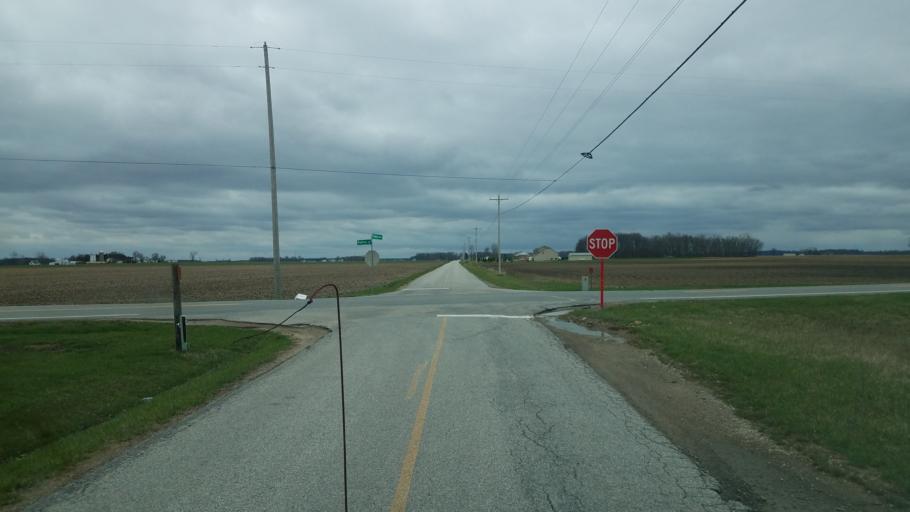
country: US
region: Ohio
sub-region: Marion County
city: Prospect
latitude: 40.3883
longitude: -83.1184
